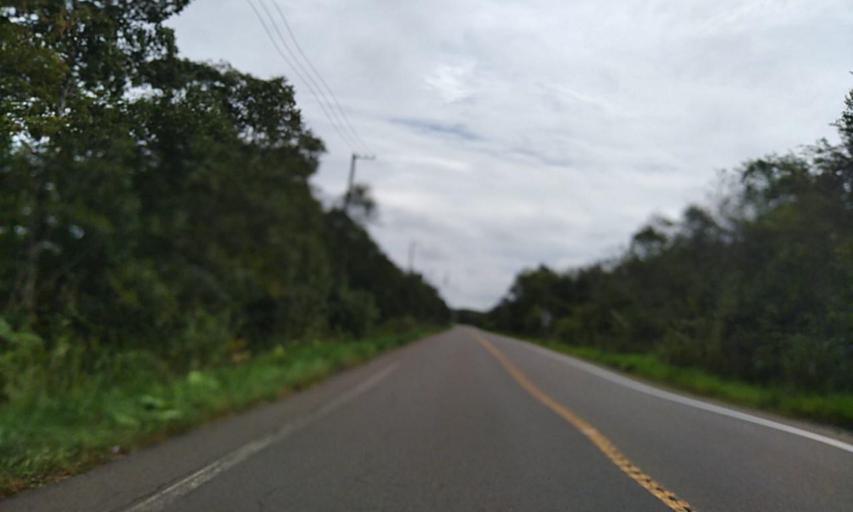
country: JP
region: Hokkaido
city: Shibetsu
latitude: 43.6133
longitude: 145.1799
